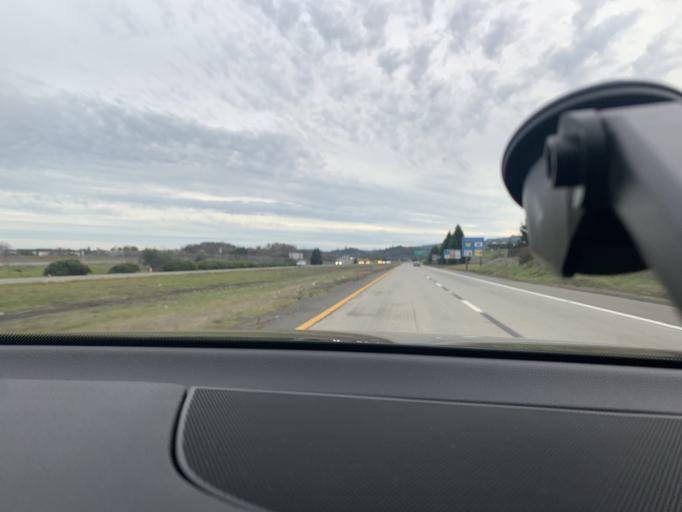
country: US
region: California
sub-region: Sonoma County
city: Cloverdale
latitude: 38.7917
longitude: -123.0116
